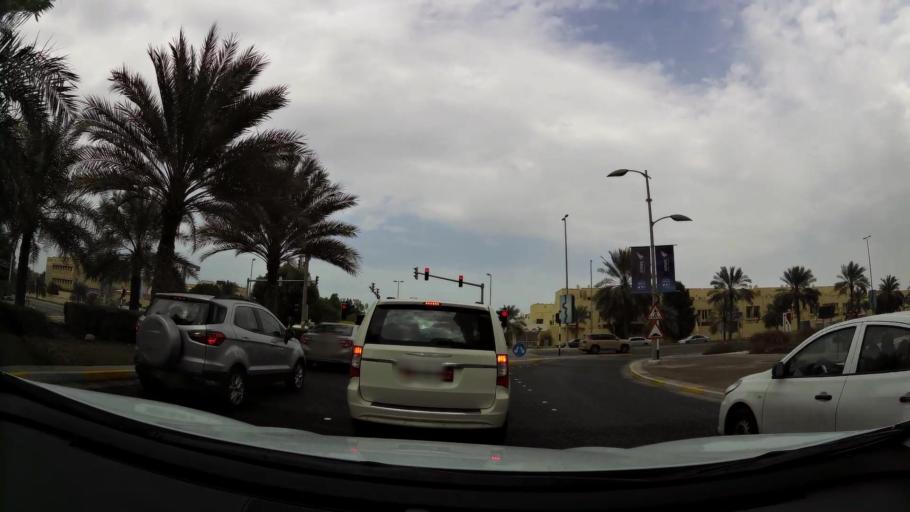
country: AE
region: Abu Dhabi
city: Abu Dhabi
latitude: 24.4210
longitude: 54.4405
